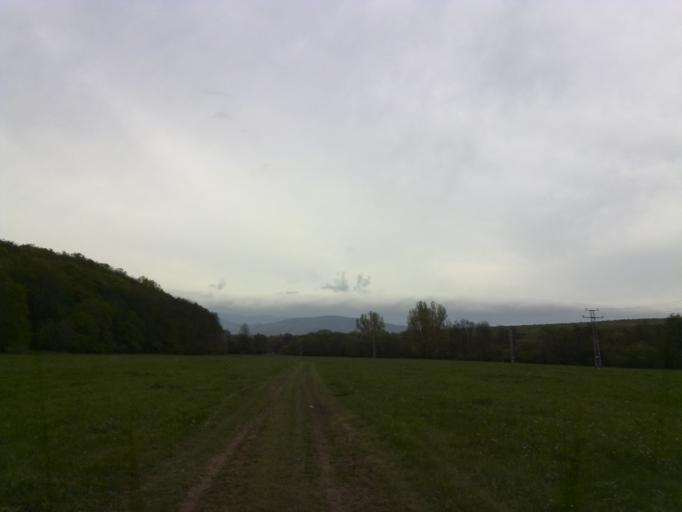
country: SK
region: Kosicky
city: Moldava nad Bodvou
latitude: 48.6483
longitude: 21.0023
